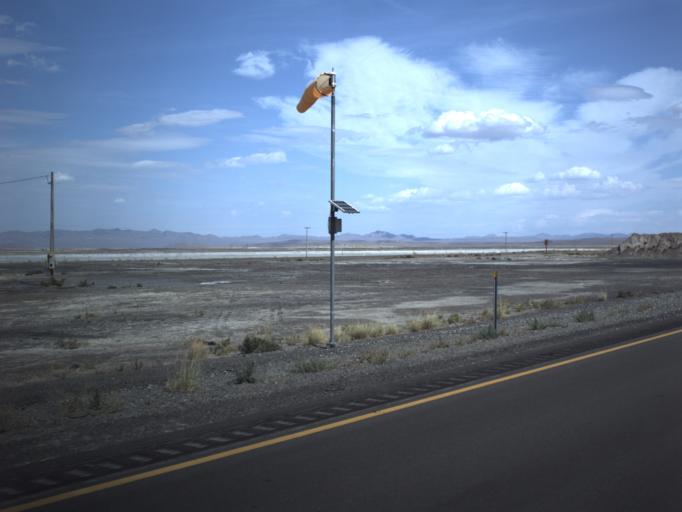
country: US
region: Utah
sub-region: Tooele County
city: Wendover
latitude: 40.7267
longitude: -113.2832
